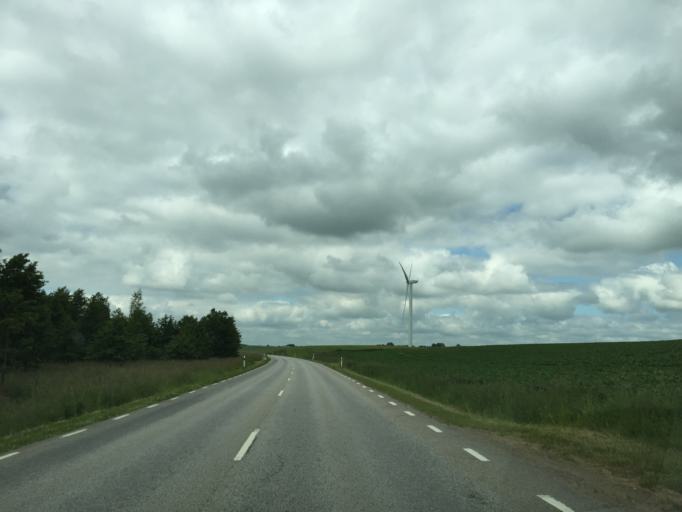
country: SE
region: Skane
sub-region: Svedala Kommun
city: Klagerup
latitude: 55.6074
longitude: 13.2660
